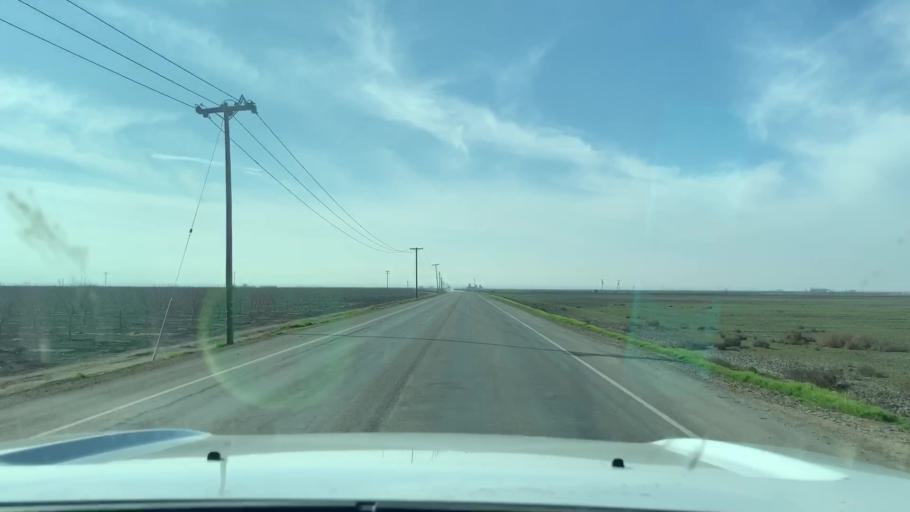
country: US
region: California
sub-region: Kern County
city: Buttonwillow
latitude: 35.4424
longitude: -119.4975
